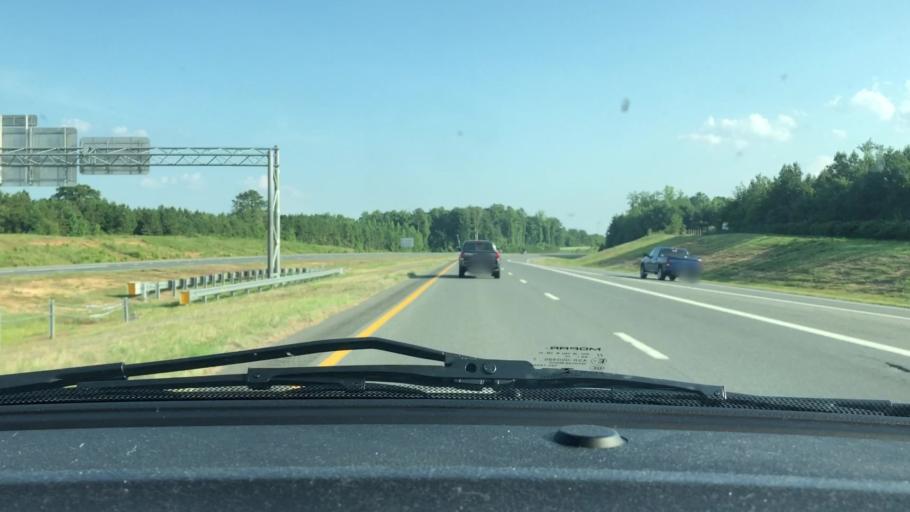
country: US
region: North Carolina
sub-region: Lee County
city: Broadway
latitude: 35.4427
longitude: -79.1193
